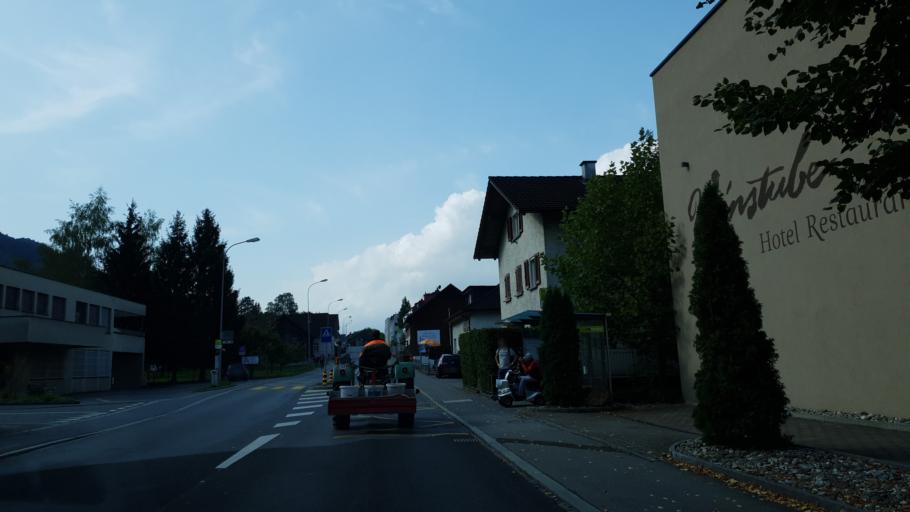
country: LI
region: Planken
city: Planken
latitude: 47.1998
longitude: 9.5442
